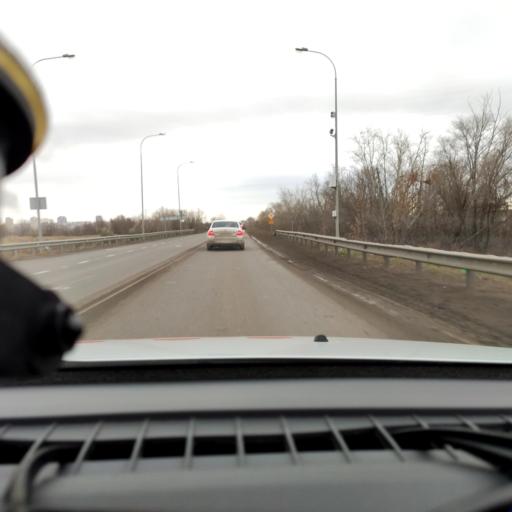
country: RU
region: Samara
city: Samara
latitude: 53.1062
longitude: 50.1353
